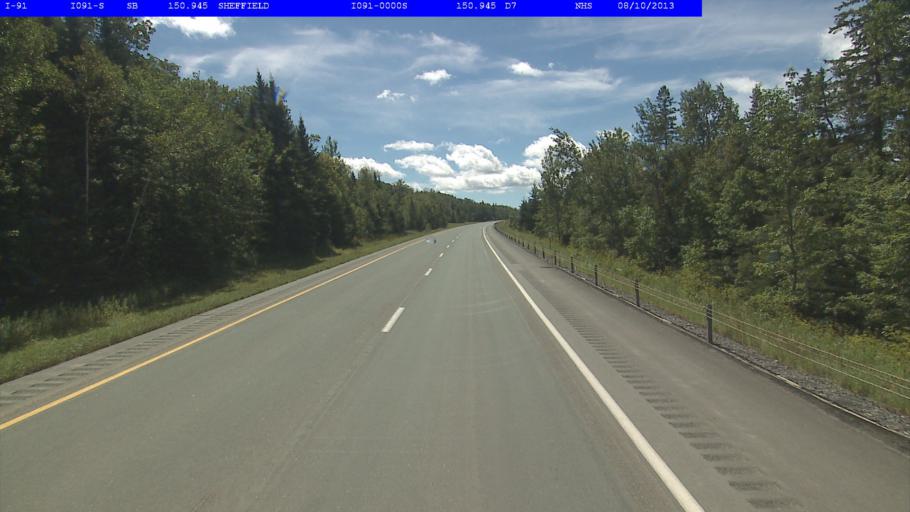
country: US
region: Vermont
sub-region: Caledonia County
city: Lyndonville
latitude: 44.6783
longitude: -72.1331
